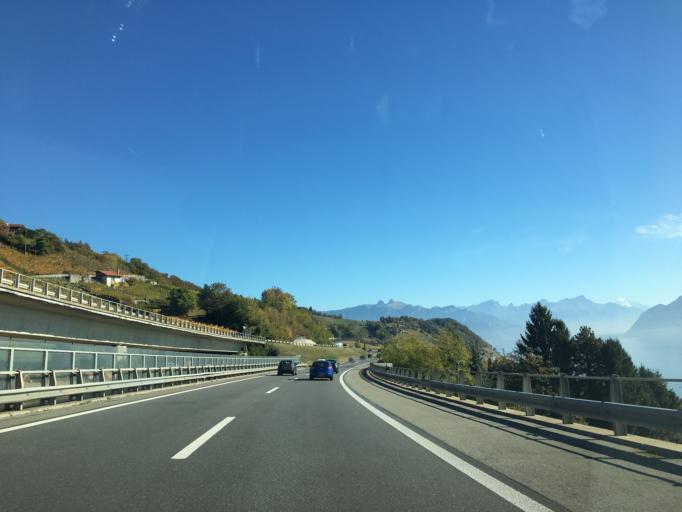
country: CH
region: Vaud
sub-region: Lavaux-Oron District
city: Cully
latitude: 46.4994
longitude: 6.7368
